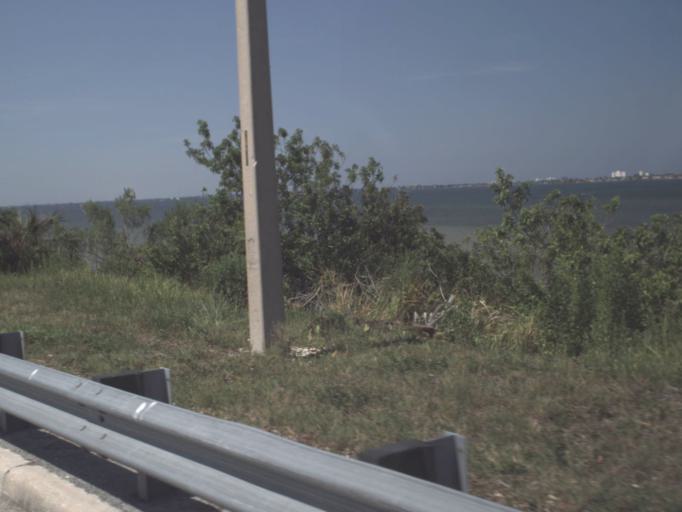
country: US
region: Florida
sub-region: Brevard County
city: Melbourne
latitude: 28.0897
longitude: -80.6078
